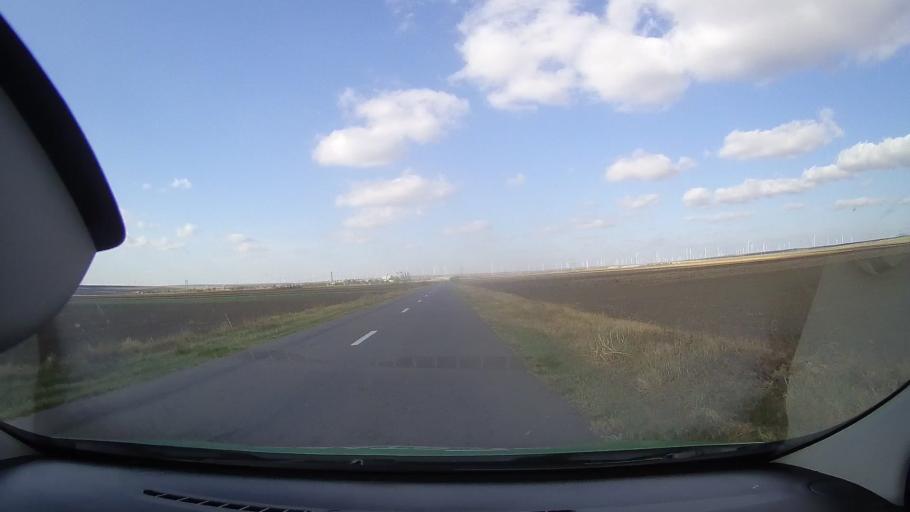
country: RO
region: Constanta
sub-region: Comuna Cogealac
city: Tariverde
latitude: 44.5527
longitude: 28.6237
